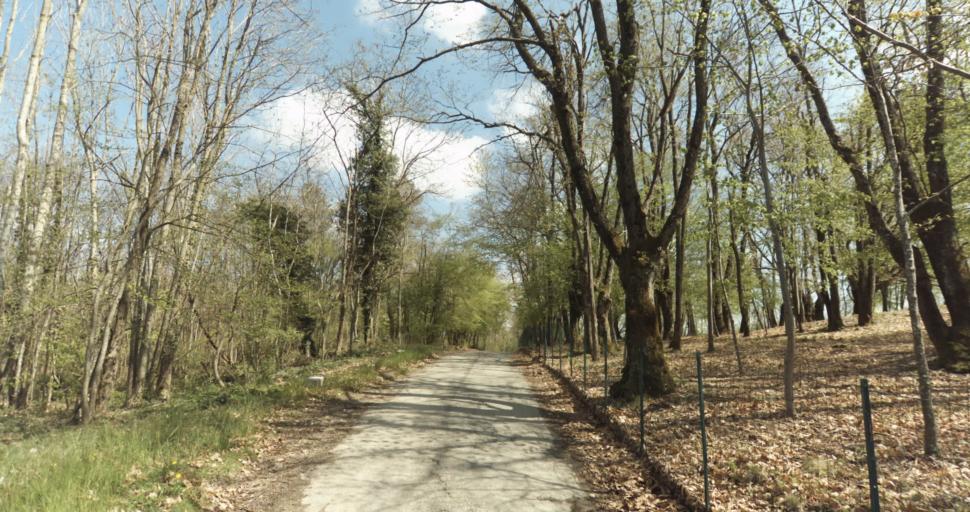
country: FR
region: Rhone-Alpes
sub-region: Departement de l'Isere
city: Saint-Marcellin
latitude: 45.1567
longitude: 5.3029
